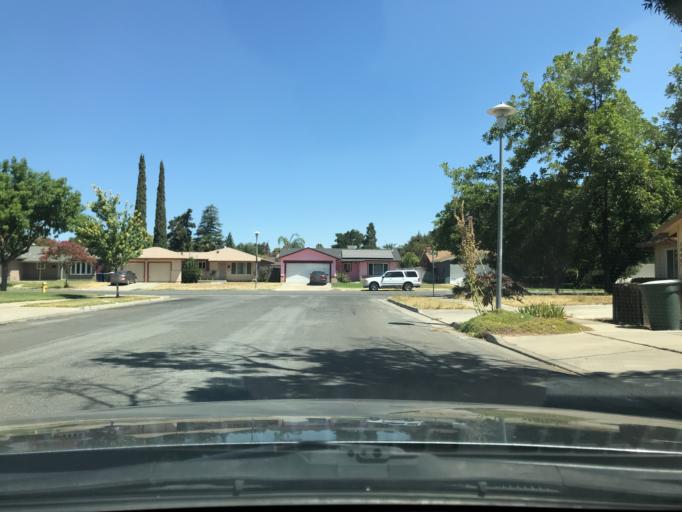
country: US
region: California
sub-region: Merced County
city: Merced
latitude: 37.3293
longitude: -120.4794
